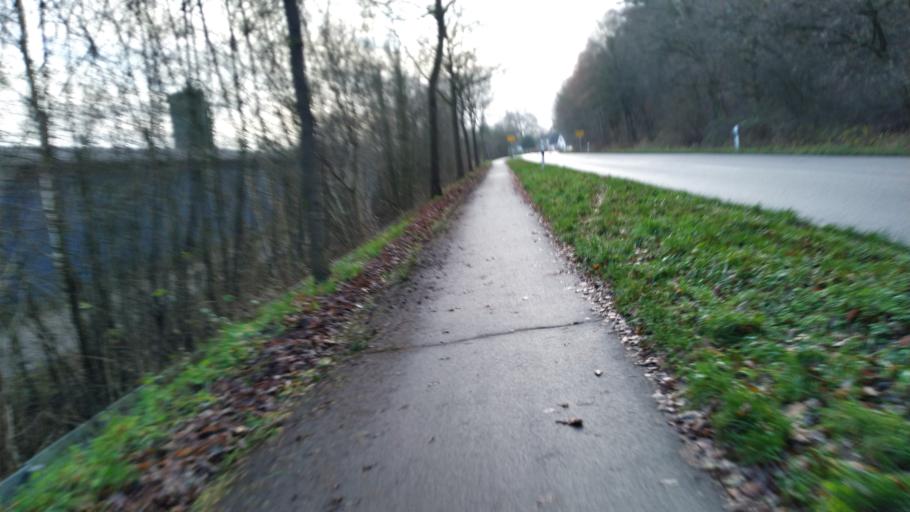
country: DE
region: Schleswig-Holstein
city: Ratekau
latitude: 53.9279
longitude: 10.7381
